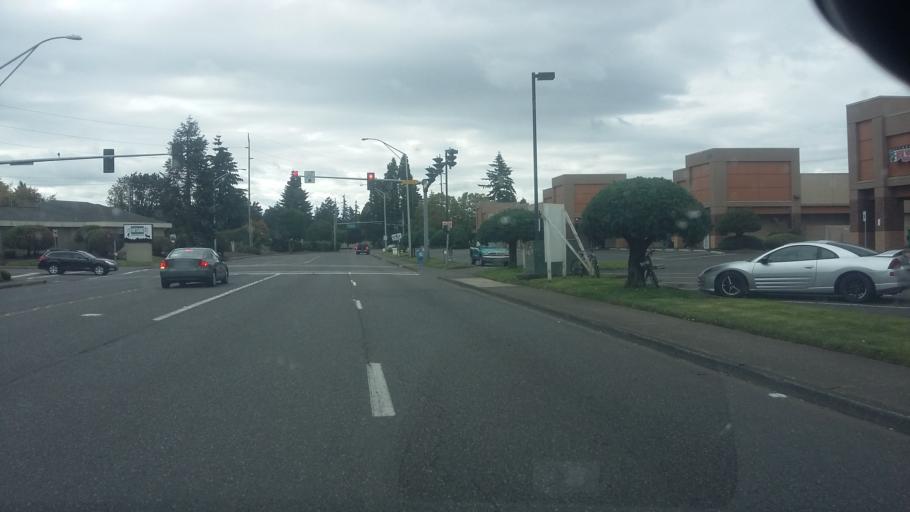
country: US
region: Washington
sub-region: Clark County
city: Orchards
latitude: 45.6164
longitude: -122.5547
